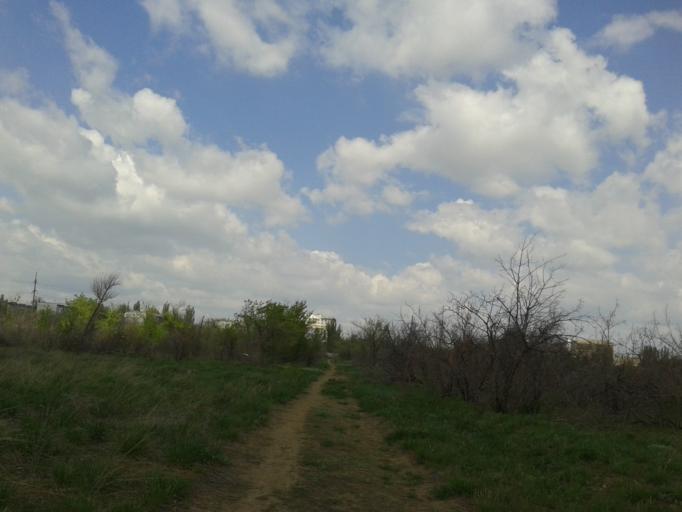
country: RU
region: Volgograd
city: Volgograd
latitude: 48.6423
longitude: 44.4372
